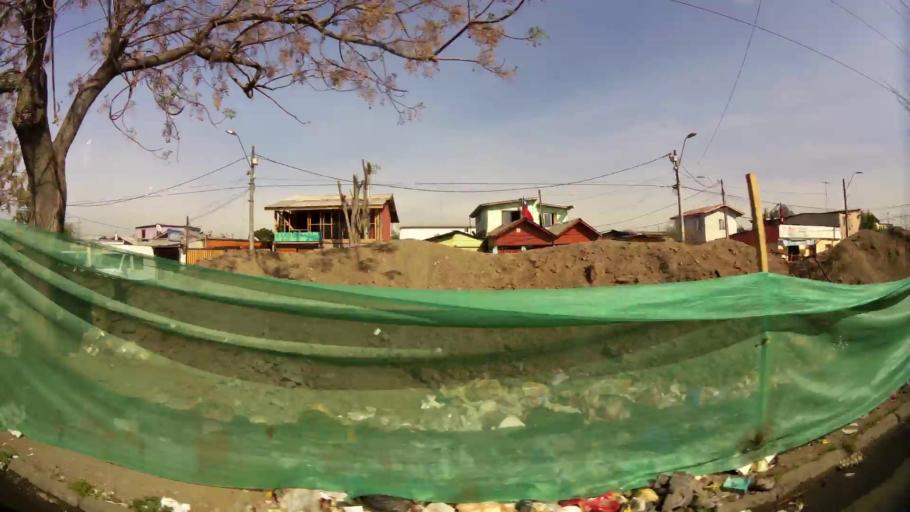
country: CL
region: Santiago Metropolitan
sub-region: Provincia de Santiago
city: Lo Prado
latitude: -33.4198
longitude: -70.7329
